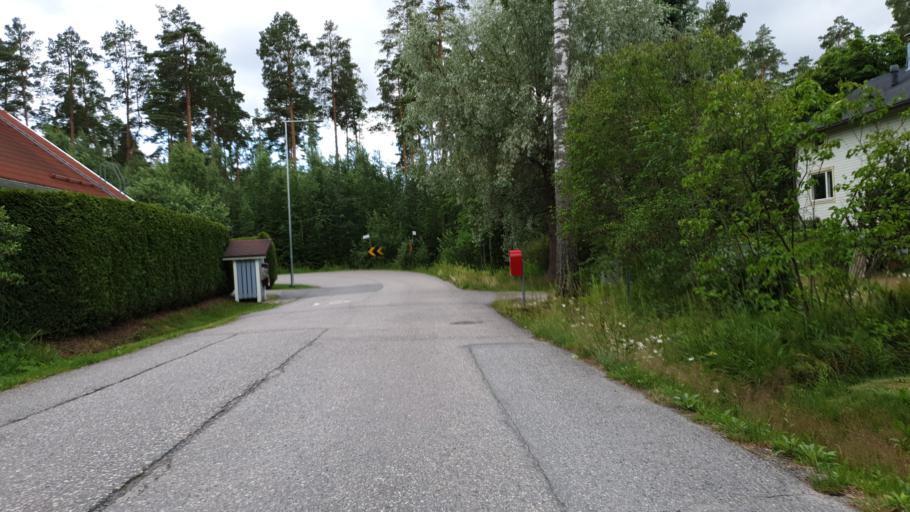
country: FI
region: Uusimaa
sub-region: Helsinki
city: Teekkarikylae
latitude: 60.2818
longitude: 24.9007
